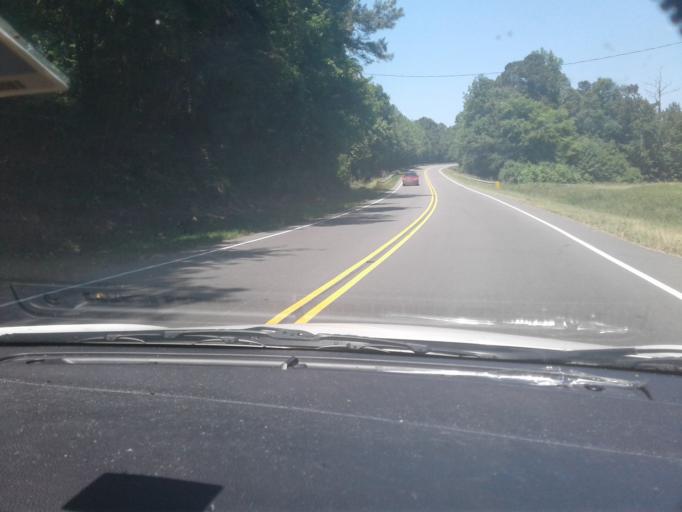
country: US
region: North Carolina
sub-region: Harnett County
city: Lillington
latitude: 35.4269
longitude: -78.8188
